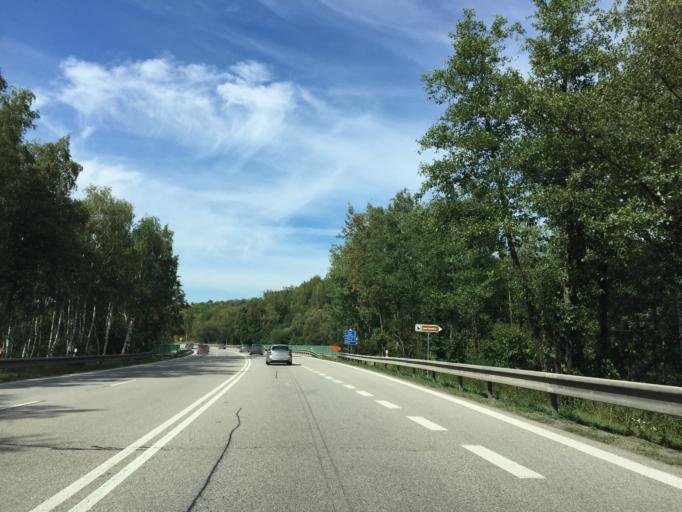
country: CZ
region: Central Bohemia
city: Votice
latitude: 49.6361
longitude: 14.6516
